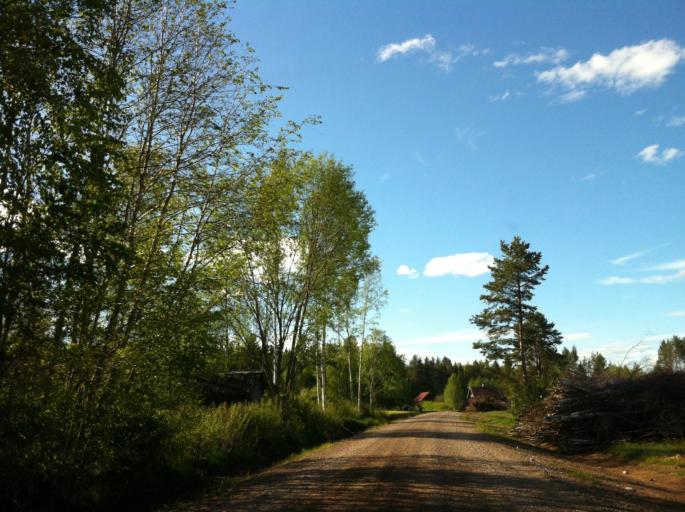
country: SE
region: Dalarna
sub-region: Leksand Municipality
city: Siljansnas
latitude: 60.7758
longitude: 14.8359
